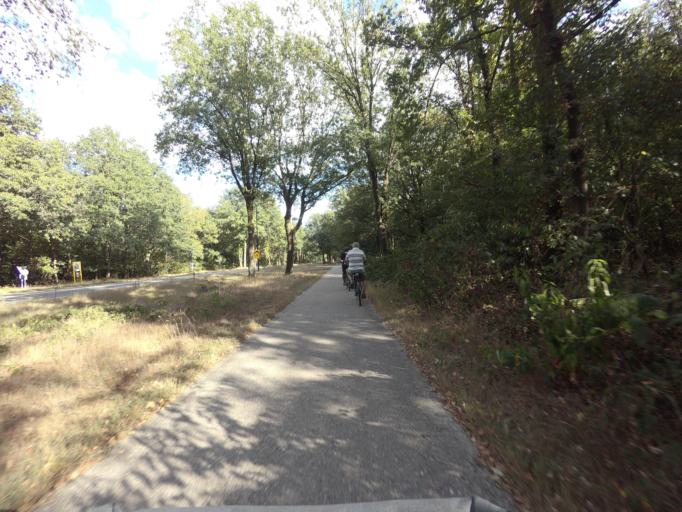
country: NL
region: North Brabant
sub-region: Gemeente Grave
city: Grave
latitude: 51.7077
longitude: 5.7523
